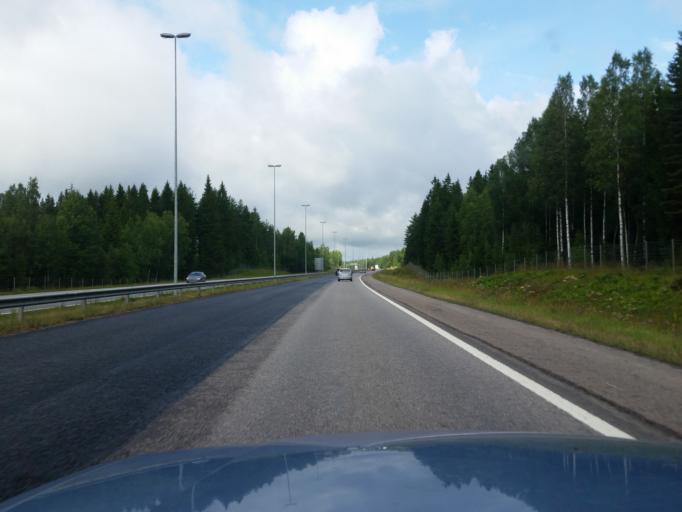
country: FI
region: Uusimaa
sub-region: Helsinki
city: Espoo
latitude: 60.2486
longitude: 24.5425
